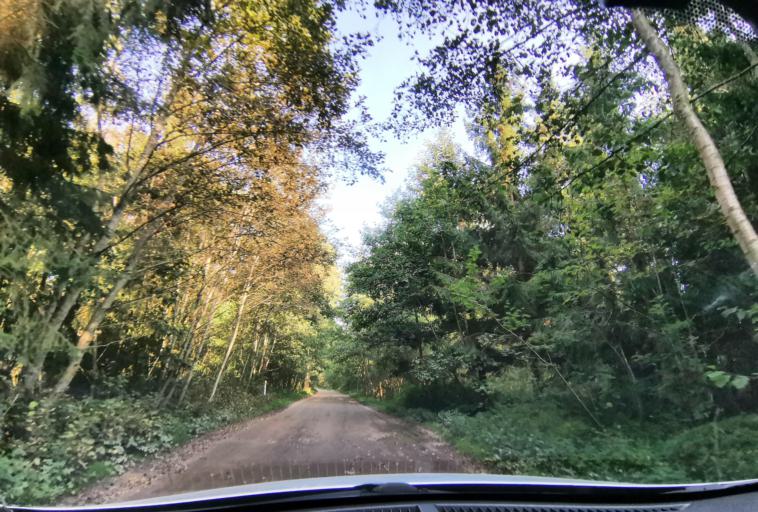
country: LT
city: Nida
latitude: 55.1627
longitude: 20.8224
